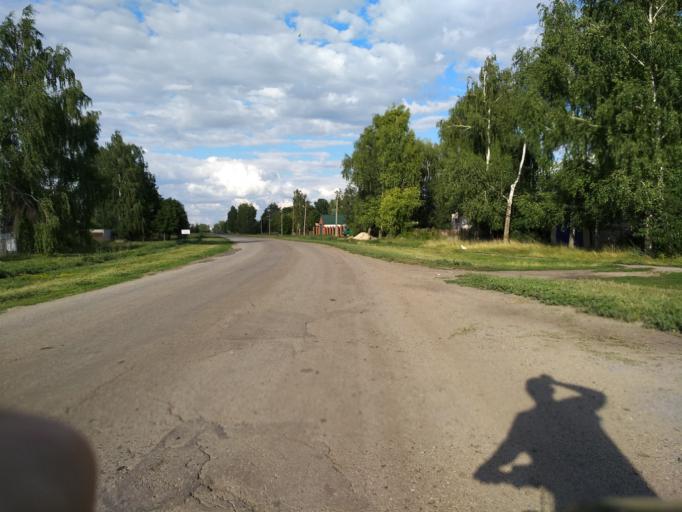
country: RU
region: Lipetsk
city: Dobrinka
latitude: 52.0355
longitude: 40.5236
